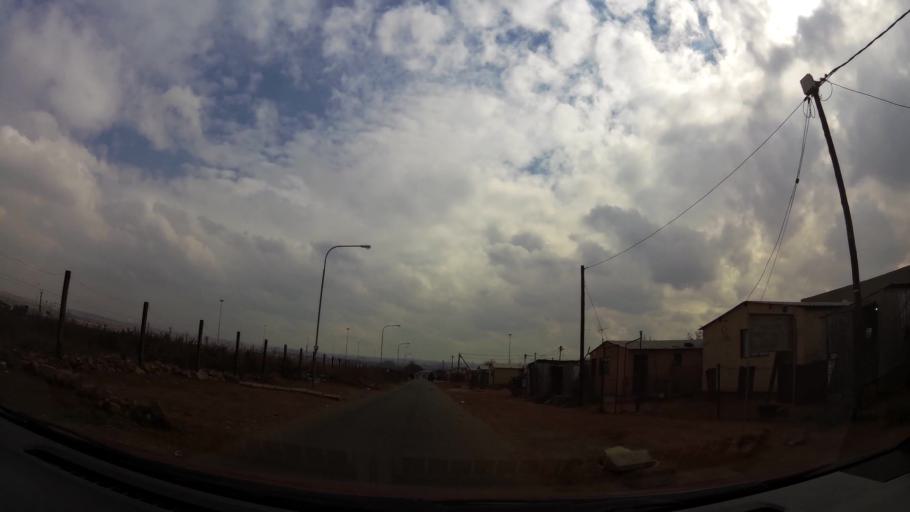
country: ZA
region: Gauteng
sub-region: City of Johannesburg Metropolitan Municipality
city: Soweto
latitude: -26.2551
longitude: 27.8205
